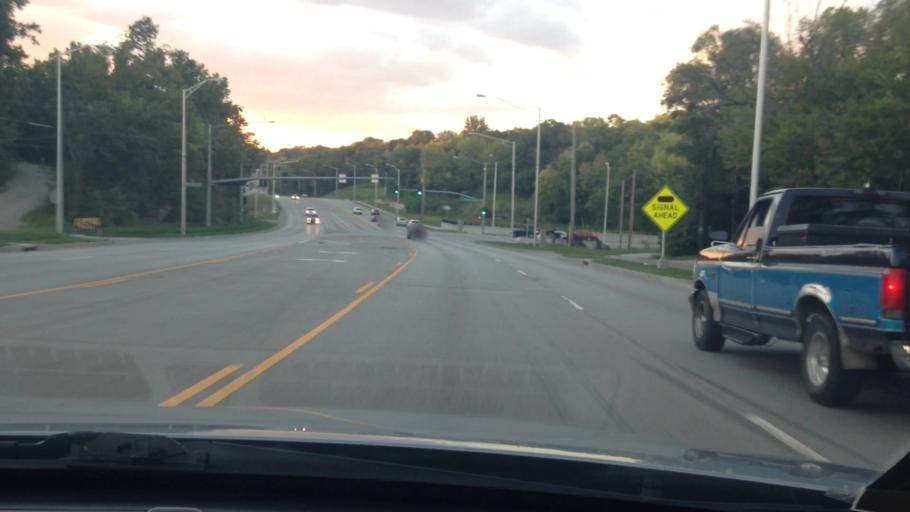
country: US
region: Missouri
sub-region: Jackson County
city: Raytown
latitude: 39.0286
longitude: -94.5078
